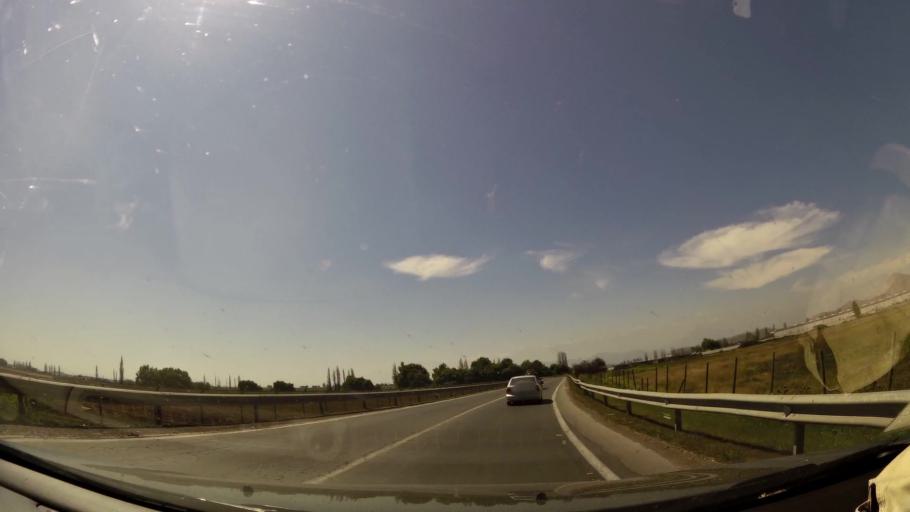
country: CL
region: Santiago Metropolitan
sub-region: Provincia de Santiago
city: Lo Prado
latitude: -33.3784
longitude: -70.7838
